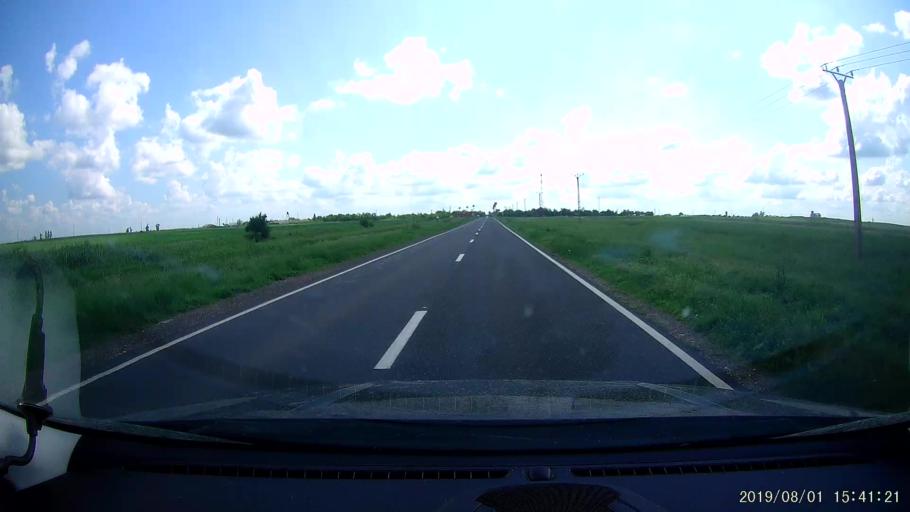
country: RO
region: Braila
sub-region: Comuna Baraganul
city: Baraganul
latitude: 44.8235
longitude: 27.5273
